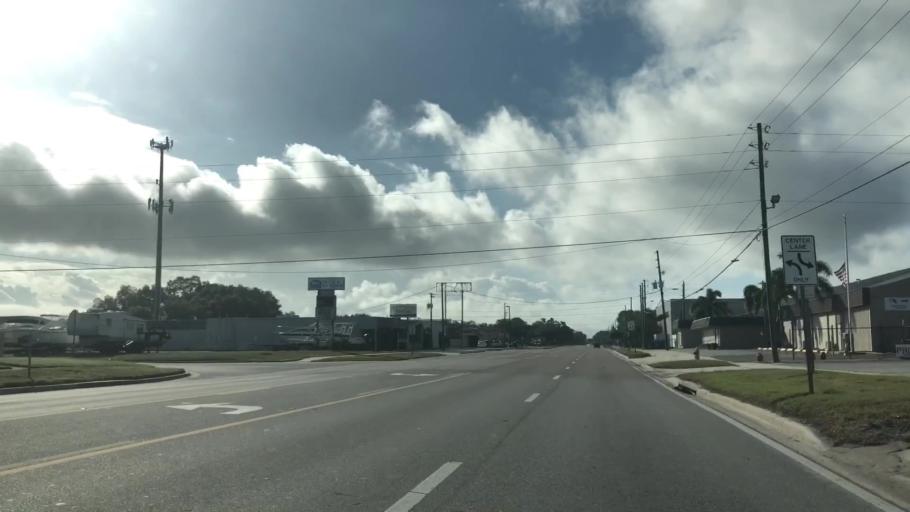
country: US
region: Florida
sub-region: Pinellas County
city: Dunedin
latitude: 27.9793
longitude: -82.7547
